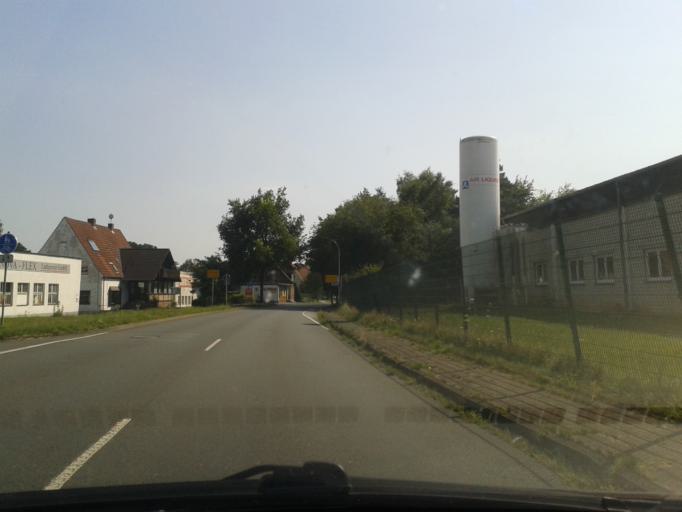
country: DE
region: North Rhine-Westphalia
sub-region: Regierungsbezirk Detmold
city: Hovelhof
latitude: 51.7997
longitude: 8.6175
